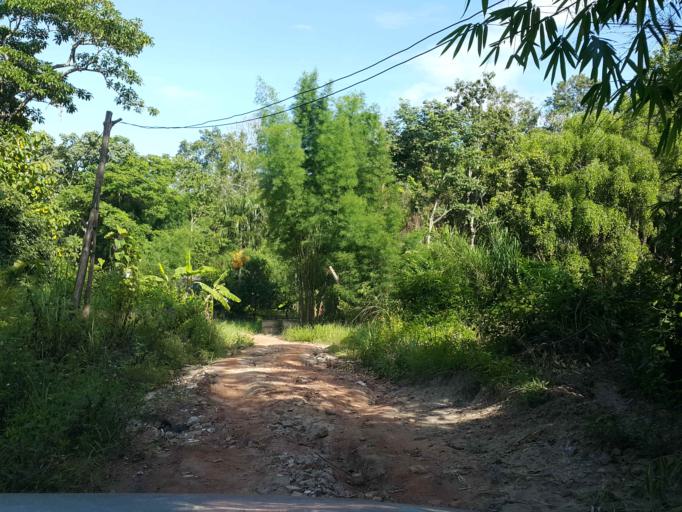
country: TH
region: Chiang Mai
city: Mae Taeng
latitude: 18.9737
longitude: 98.8881
